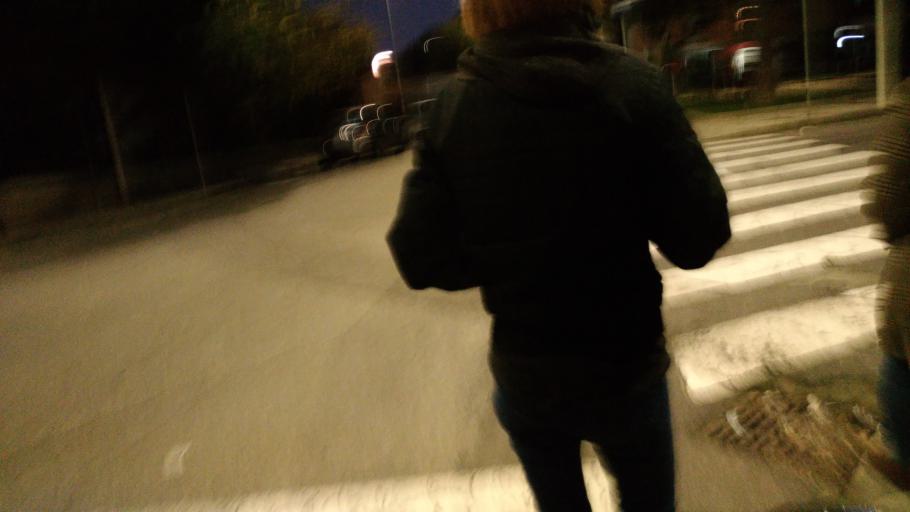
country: IT
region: Sardinia
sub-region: Provincia di Cagliari
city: Su Planu
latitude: 39.2392
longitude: 9.1042
